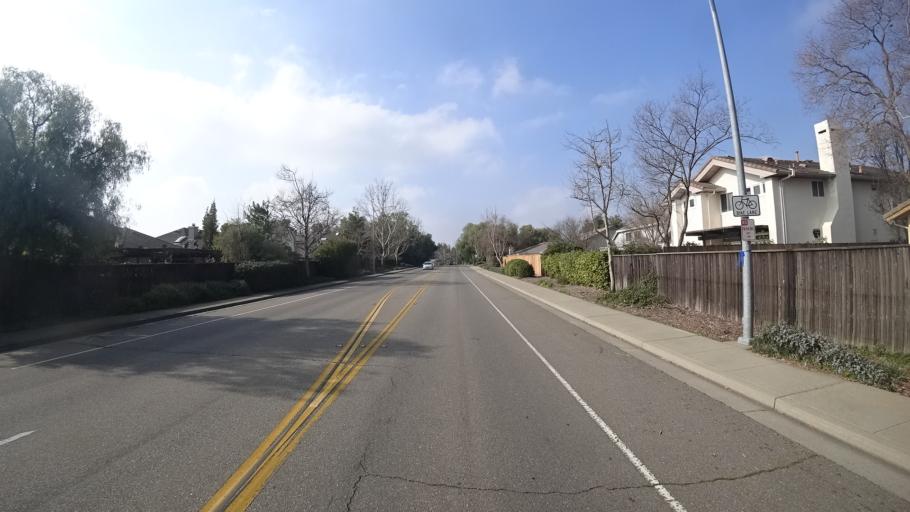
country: US
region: California
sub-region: Yolo County
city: Davis
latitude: 38.5736
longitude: -121.7522
